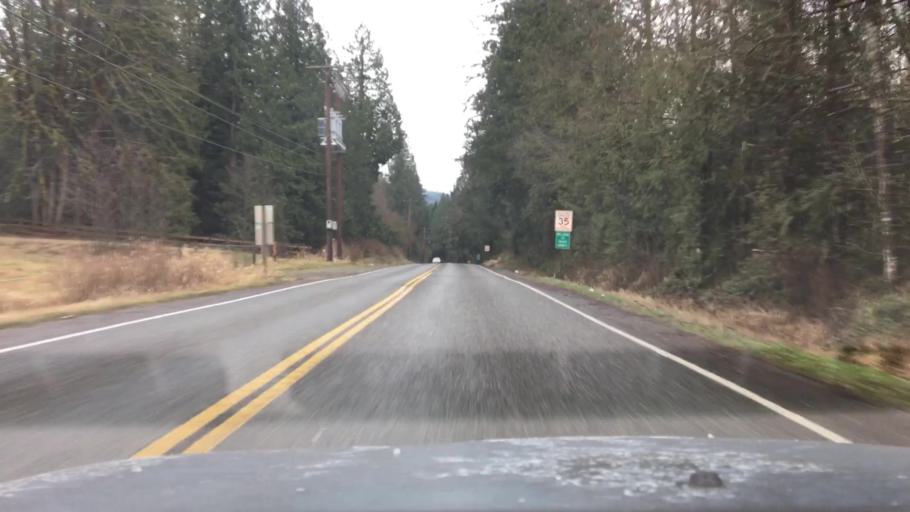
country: US
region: Washington
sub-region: Whatcom County
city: Sudden Valley
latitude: 48.6454
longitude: -122.3235
